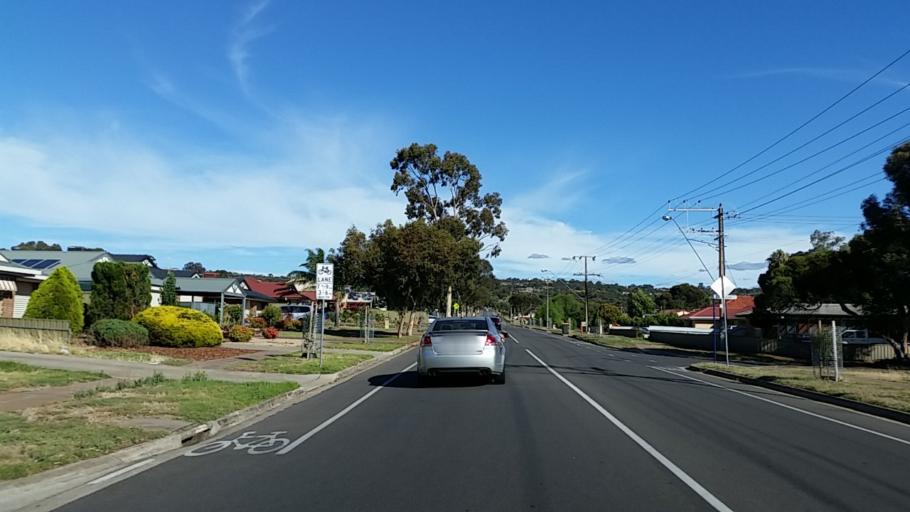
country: AU
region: South Australia
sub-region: Salisbury
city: Salisbury
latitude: -34.7859
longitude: 138.6588
